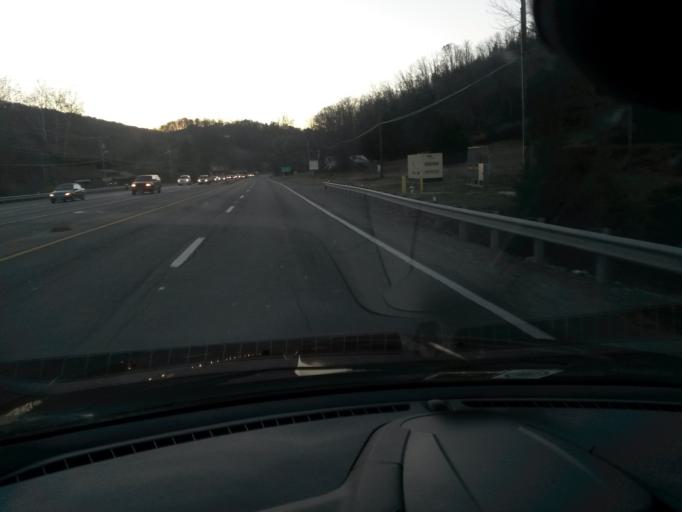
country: US
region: Virginia
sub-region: Roanoke County
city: Narrows
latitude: 37.2029
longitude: -79.9495
